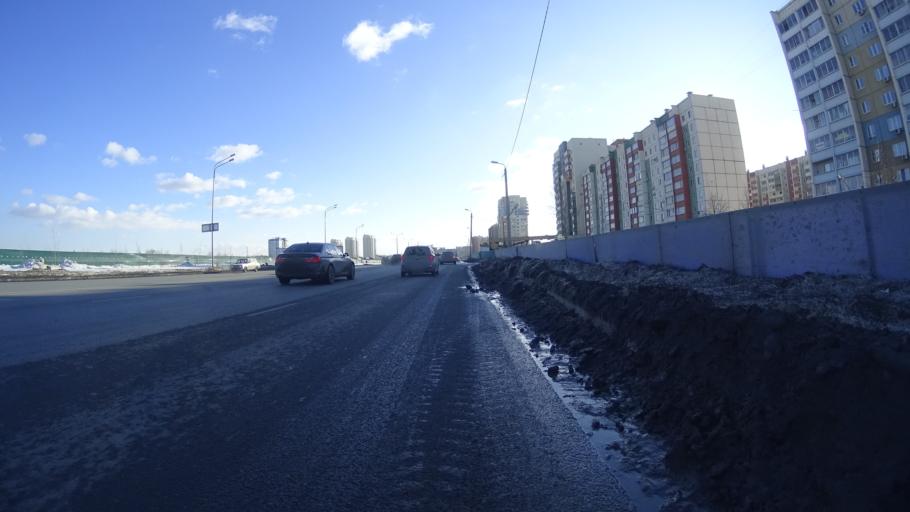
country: RU
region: Chelyabinsk
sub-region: Gorod Chelyabinsk
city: Chelyabinsk
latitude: 55.1660
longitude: 61.3023
